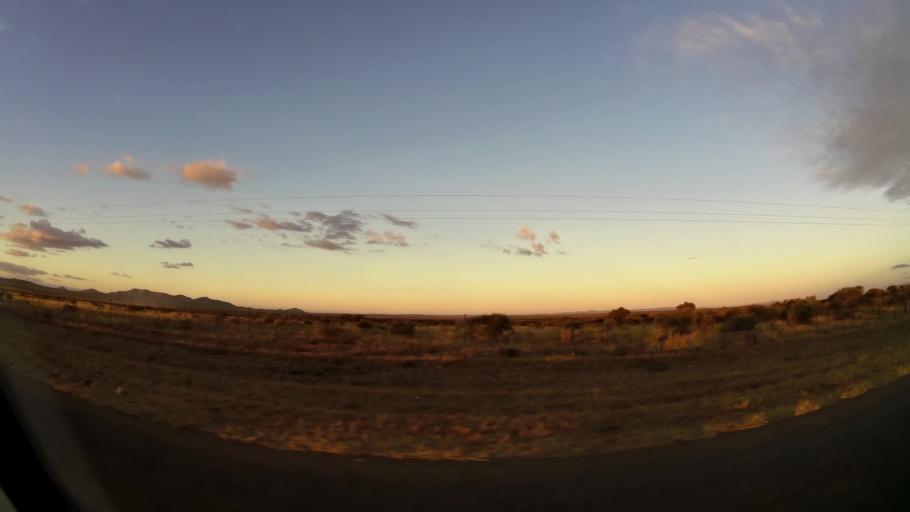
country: ZA
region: Limpopo
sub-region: Capricorn District Municipality
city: Polokwane
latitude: -23.7610
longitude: 29.4739
